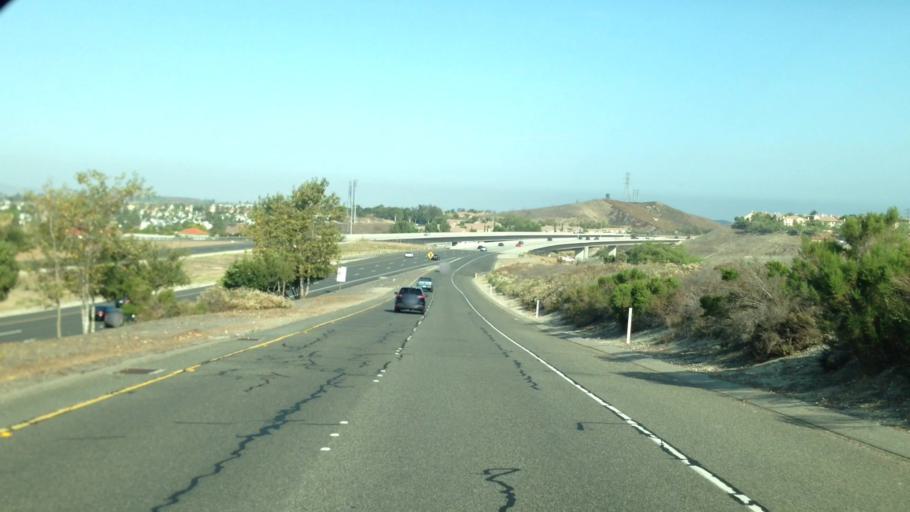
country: US
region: California
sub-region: Orange County
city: Portola Hills
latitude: 33.6558
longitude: -117.6257
